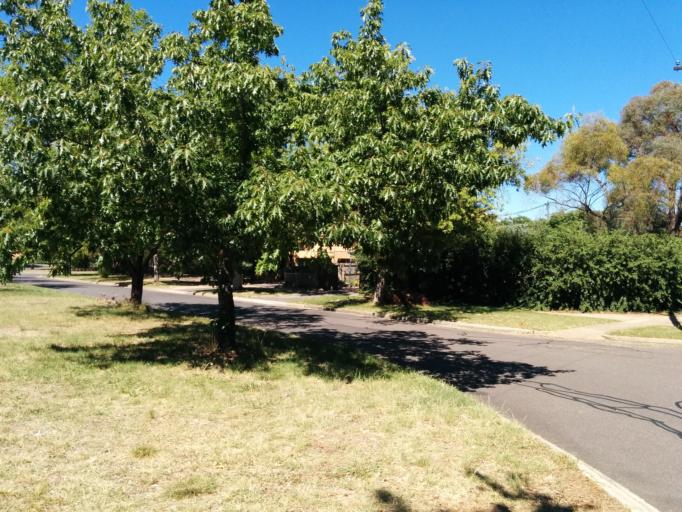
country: AU
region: Australian Capital Territory
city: Acton
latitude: -35.2568
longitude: 149.1275
